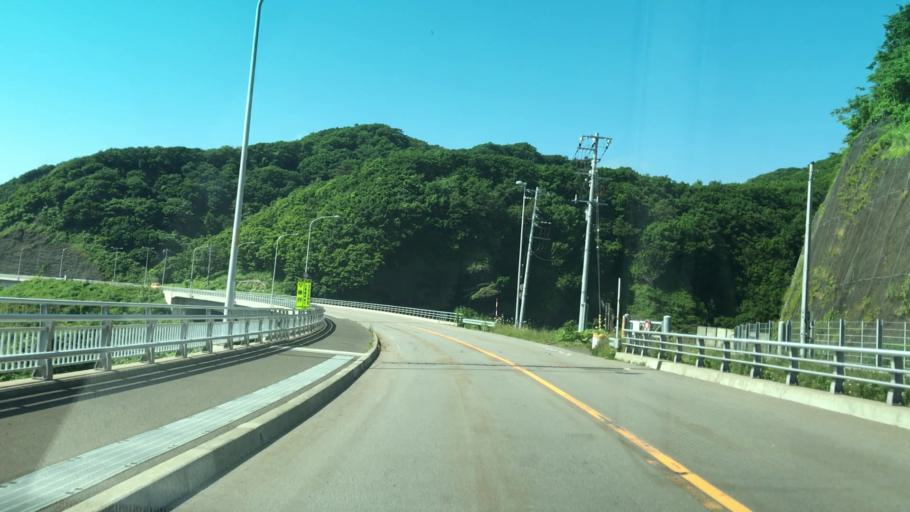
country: JP
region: Hokkaido
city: Iwanai
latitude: 43.1264
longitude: 140.4426
